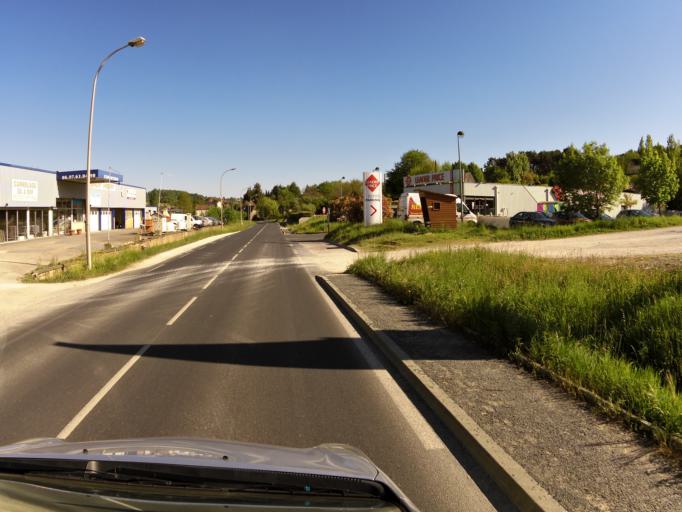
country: FR
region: Aquitaine
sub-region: Departement de la Dordogne
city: Sarlat-la-Caneda
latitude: 44.9059
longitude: 1.2072
